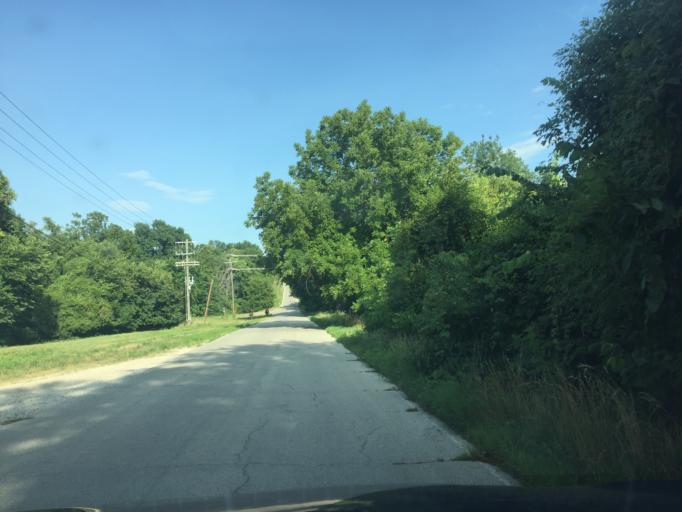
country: US
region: Kansas
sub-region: Leavenworth County
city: Leavenworth
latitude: 39.3600
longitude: -94.9282
